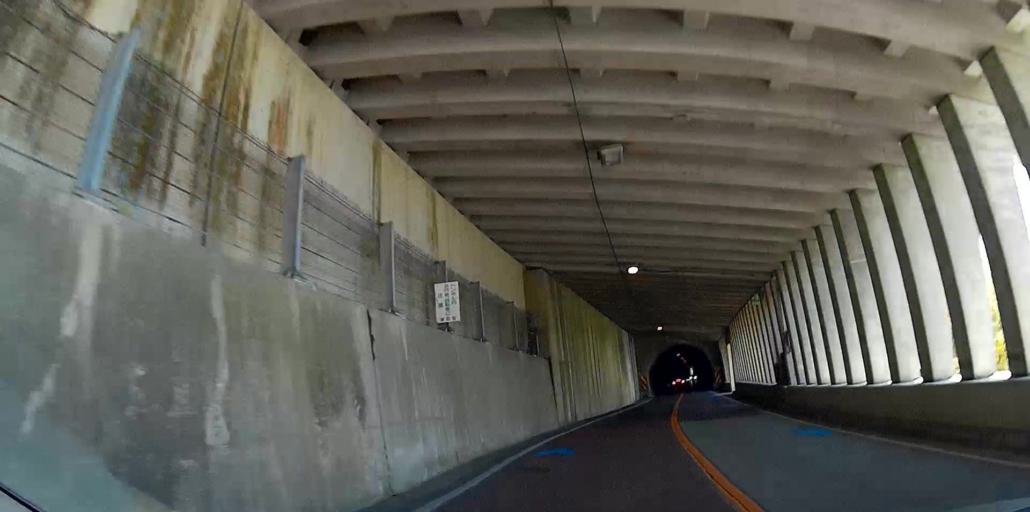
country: JP
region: Chiba
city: Futtsu
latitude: 35.1531
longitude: 139.8259
